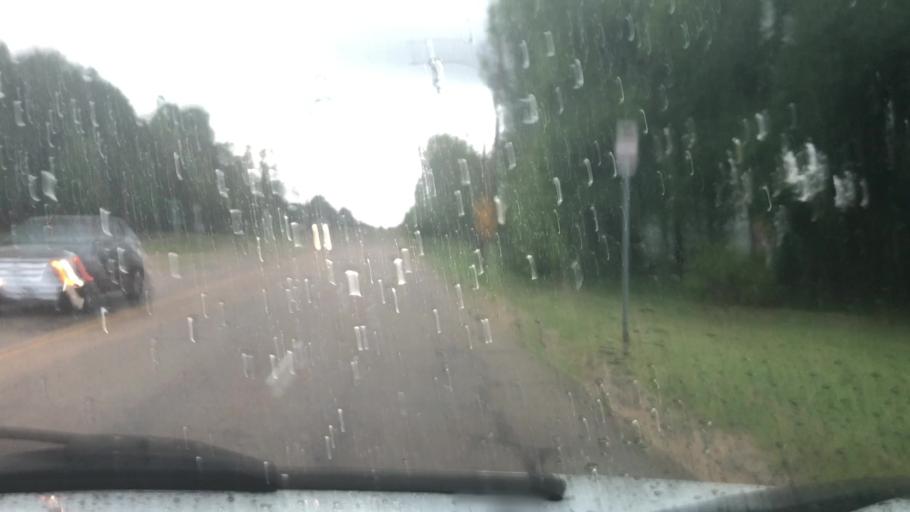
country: US
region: Texas
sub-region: Bowie County
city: Wake Village
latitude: 33.4064
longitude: -94.0792
